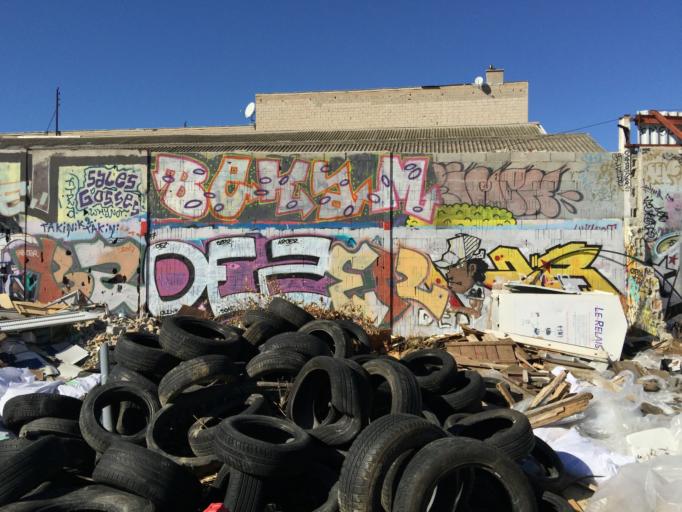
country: FR
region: Provence-Alpes-Cote d'Azur
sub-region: Departement des Bouches-du-Rhone
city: Marseille 10
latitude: 43.2758
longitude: 5.4086
